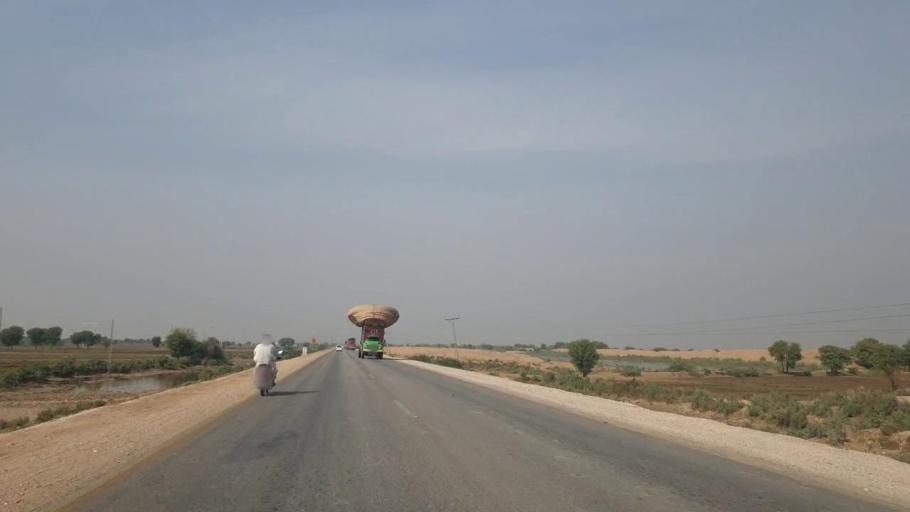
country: PK
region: Sindh
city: Sann
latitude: 26.0705
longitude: 68.0992
